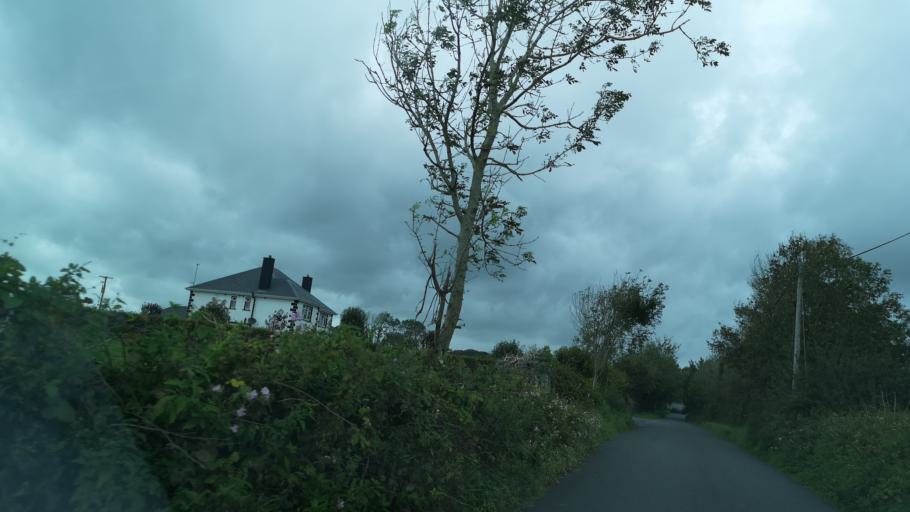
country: IE
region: Connaught
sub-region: County Galway
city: Athenry
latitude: 53.2749
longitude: -8.6828
